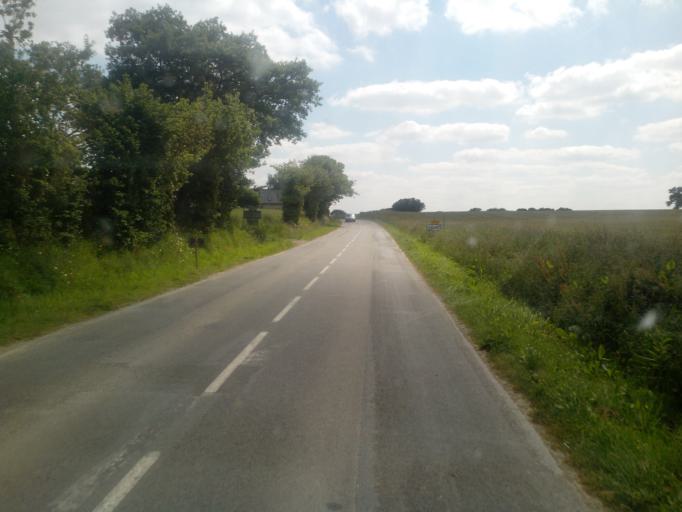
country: FR
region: Brittany
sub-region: Departement d'Ille-et-Vilaine
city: Montreuil-sur-Ille
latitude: 48.3250
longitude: -1.6448
